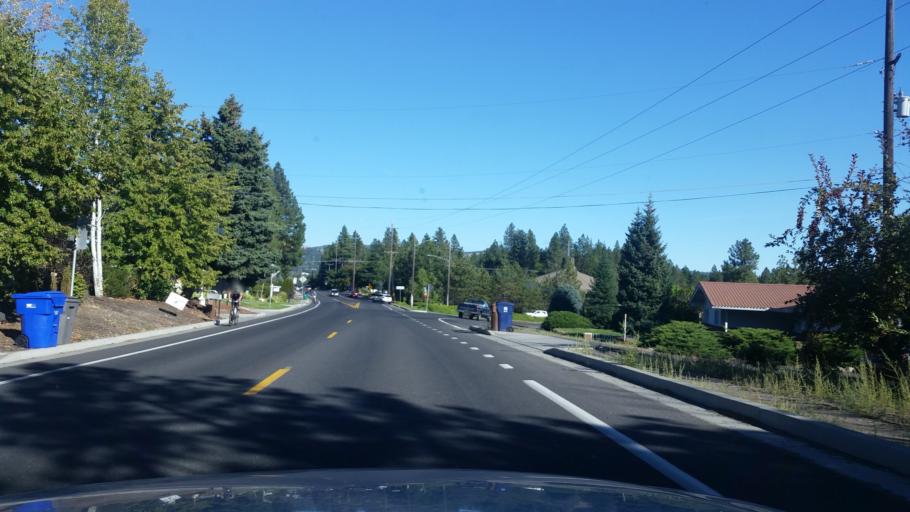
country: US
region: Washington
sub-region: Spokane County
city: Spokane
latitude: 47.6024
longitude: -117.3938
